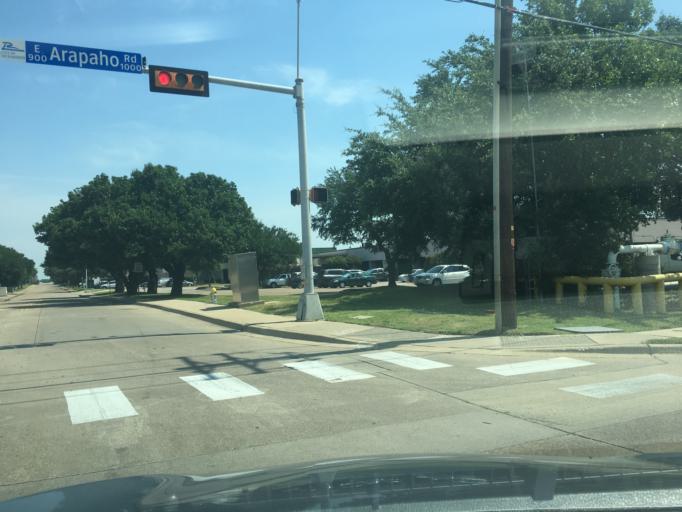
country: US
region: Texas
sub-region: Dallas County
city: Richardson
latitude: 32.9607
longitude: -96.7094
